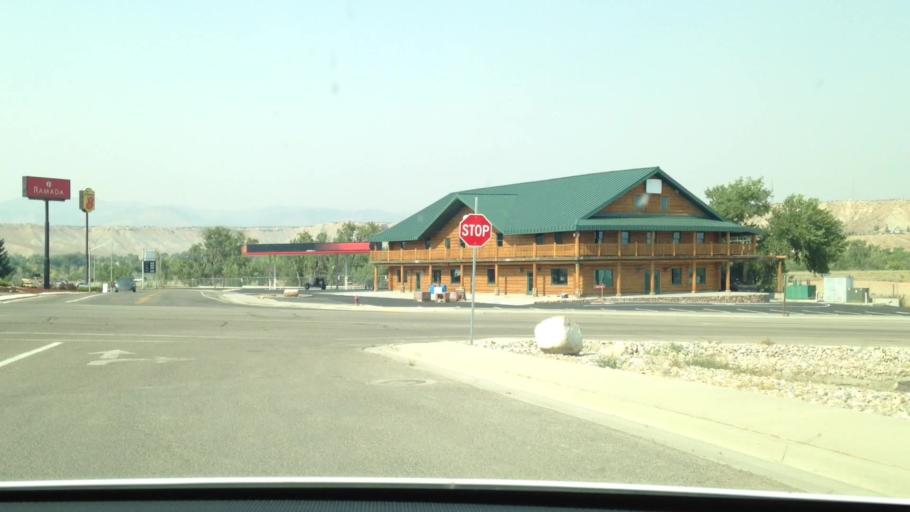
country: US
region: Utah
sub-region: Carbon County
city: Carbonville
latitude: 39.6009
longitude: -110.8311
